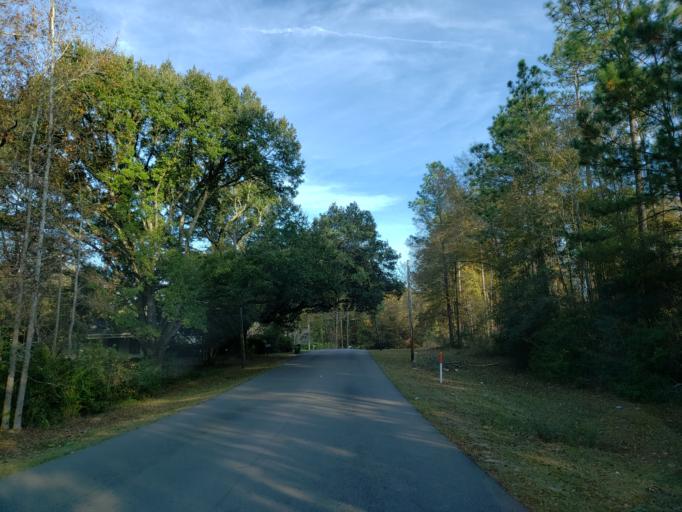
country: US
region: Mississippi
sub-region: Forrest County
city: Hattiesburg
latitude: 31.2992
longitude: -89.3219
